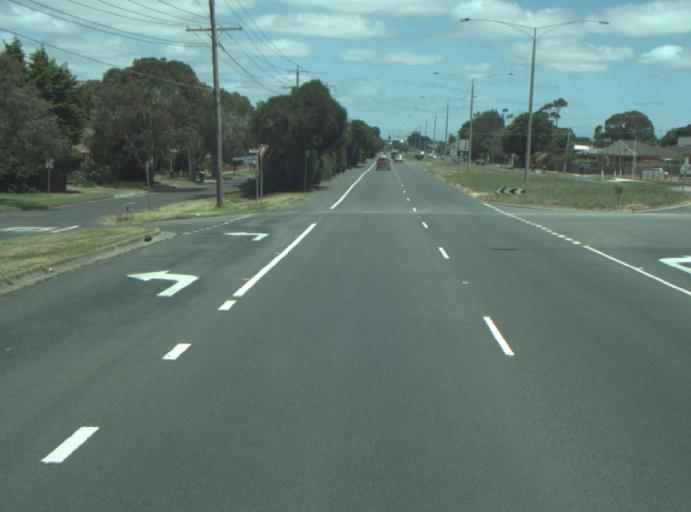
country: AU
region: Victoria
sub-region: Greater Geelong
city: Wandana Heights
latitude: -38.1825
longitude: 144.3351
